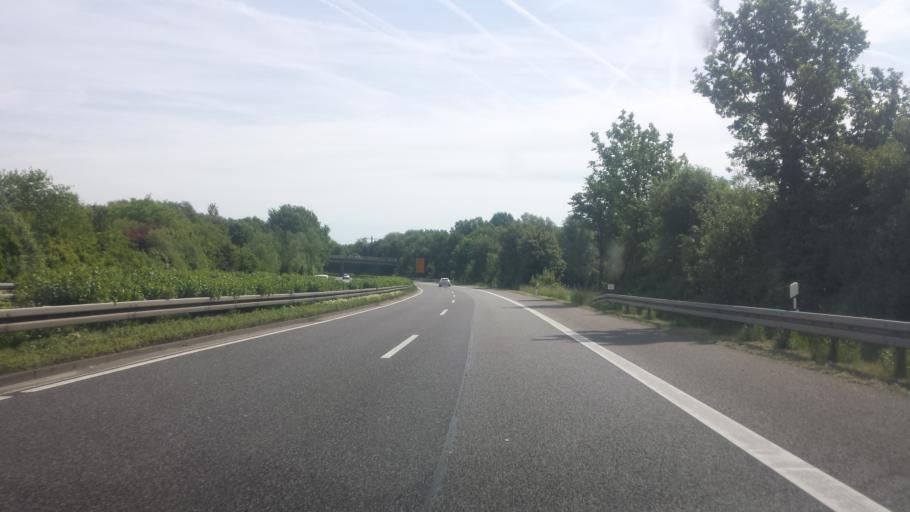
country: DE
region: Hesse
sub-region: Regierungsbezirk Darmstadt
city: Bad Vilbel
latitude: 50.1807
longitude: 8.7187
